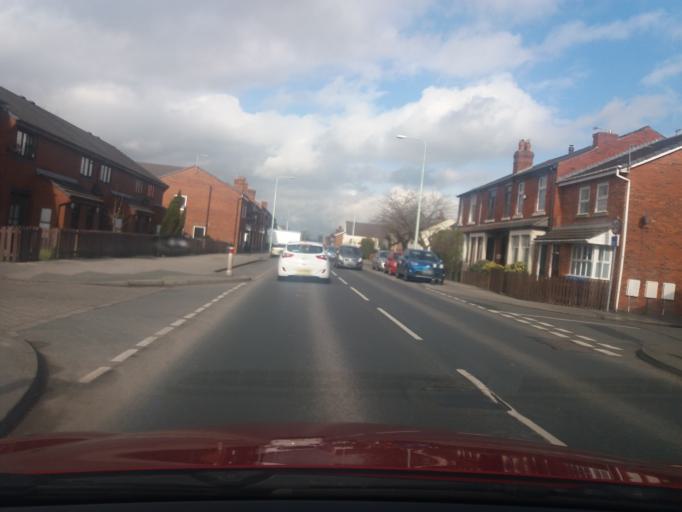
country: GB
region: England
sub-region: Lancashire
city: Chorley
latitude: 53.6421
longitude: -2.6389
